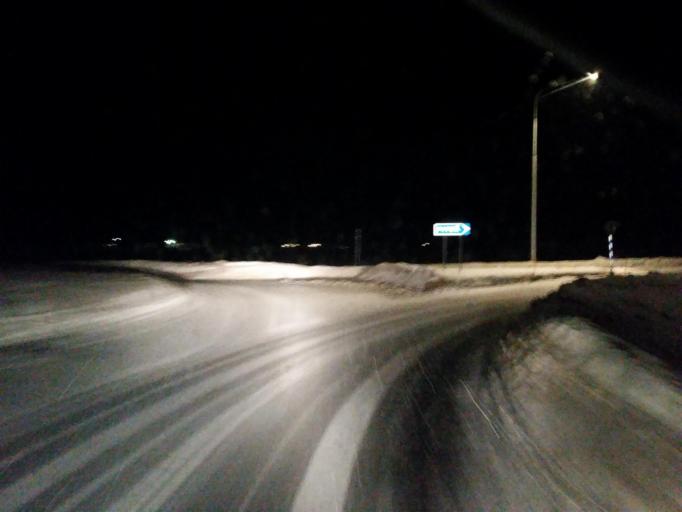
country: SE
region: Norrbotten
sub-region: Alvsbyns Kommun
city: AElvsbyn
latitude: 65.6687
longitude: 21.0463
